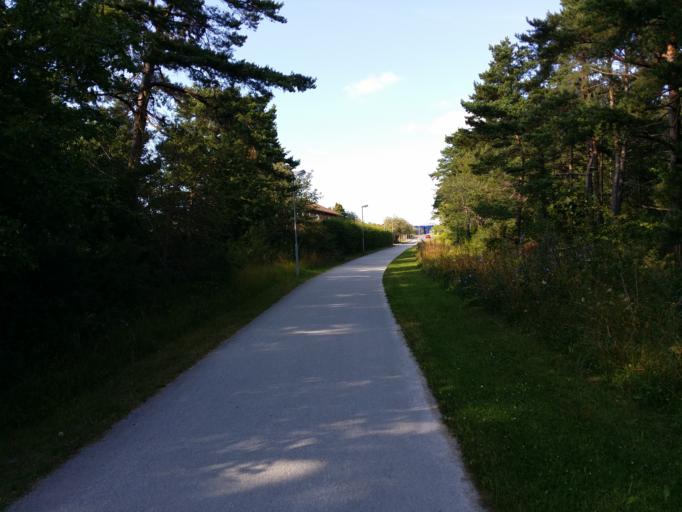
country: SE
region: Gotland
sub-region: Gotland
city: Visby
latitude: 57.6291
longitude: 18.3234
